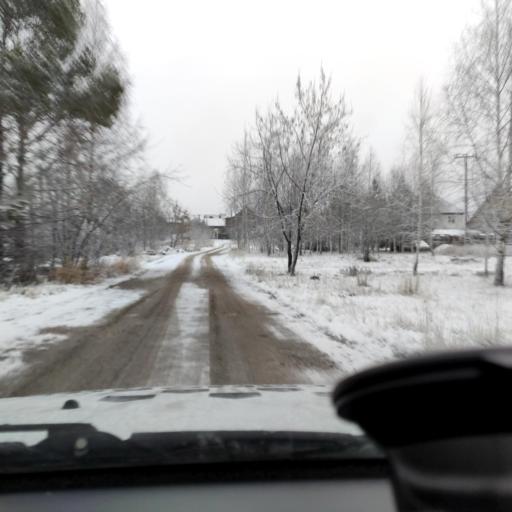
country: RU
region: Perm
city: Perm
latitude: 58.0392
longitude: 56.3621
